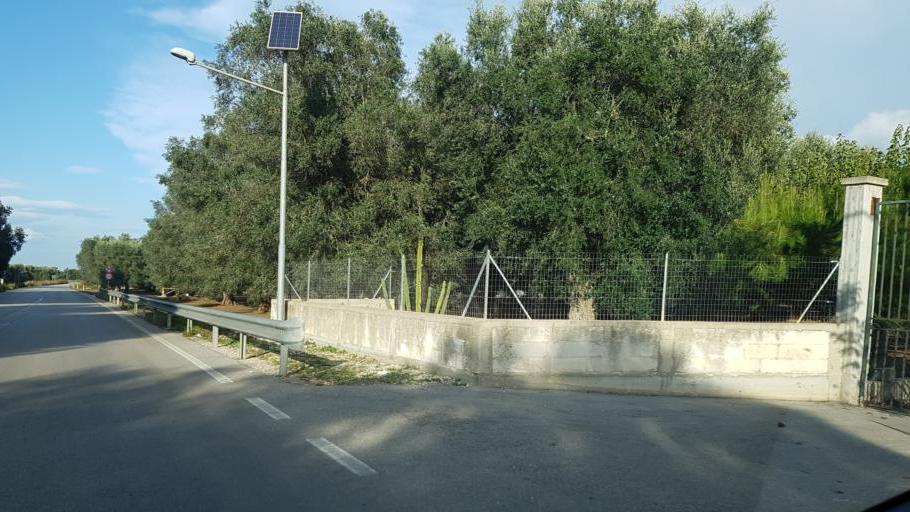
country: IT
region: Apulia
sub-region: Provincia di Brindisi
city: Oria
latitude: 40.5279
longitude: 17.6543
